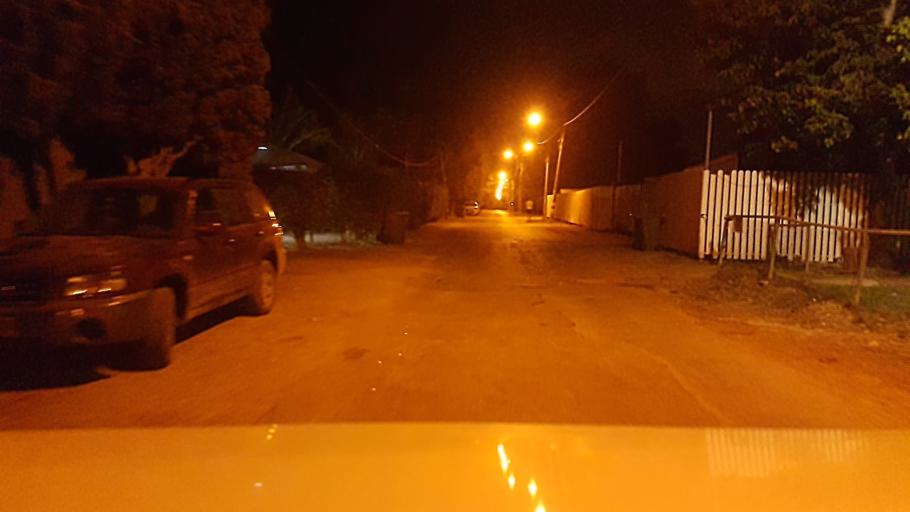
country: IL
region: Central District
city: Nehalim
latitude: 32.0801
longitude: 34.9260
